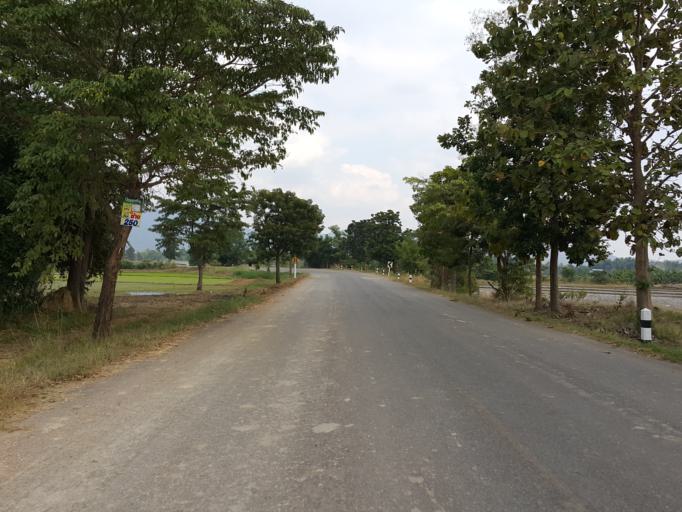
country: TH
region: Sukhothai
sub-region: Amphoe Si Satchanalai
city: Si Satchanalai
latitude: 17.4672
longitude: 99.6390
